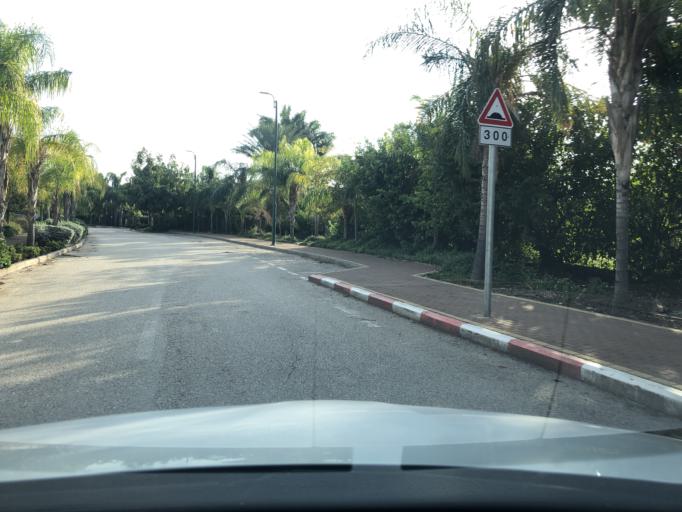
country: IL
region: Northern District
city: Yavne'el
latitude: 32.6584
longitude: 35.5768
